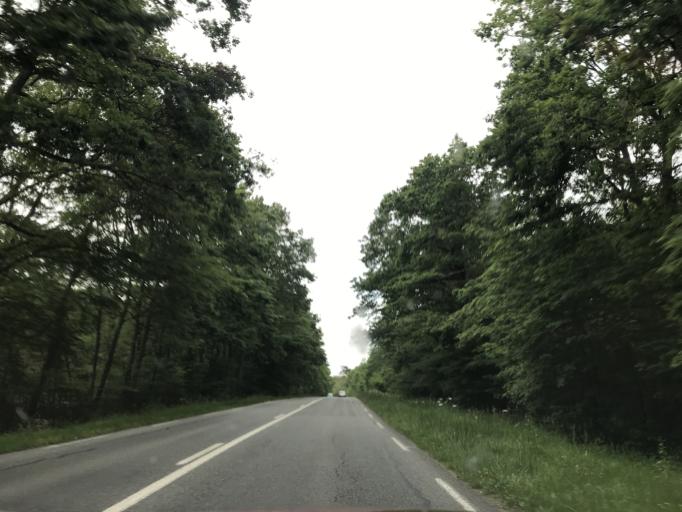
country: FR
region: Auvergne
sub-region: Departement du Puy-de-Dome
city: Randan
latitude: 46.0301
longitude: 3.3568
